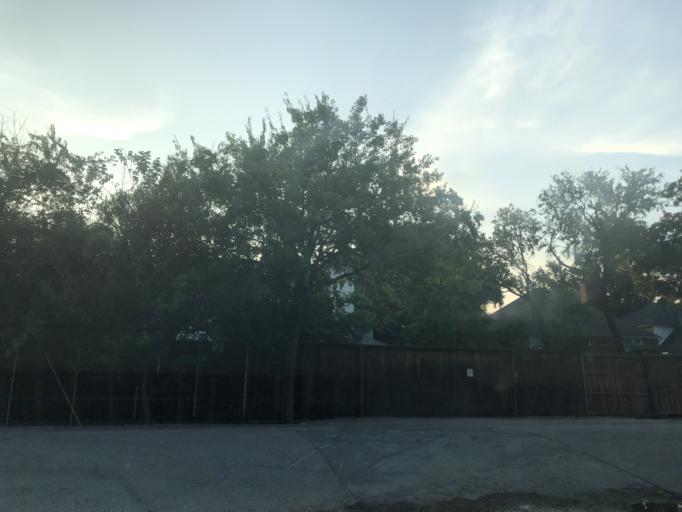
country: US
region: Texas
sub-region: Dallas County
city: Dallas
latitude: 32.7561
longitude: -96.8357
